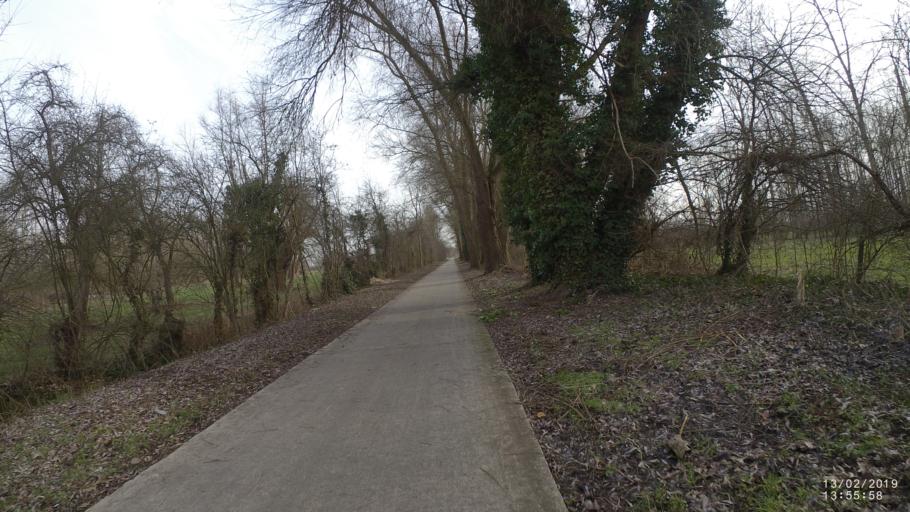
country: BE
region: Flanders
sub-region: Provincie Vlaams-Brabant
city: Zoutleeuw
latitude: 50.8253
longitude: 5.1110
